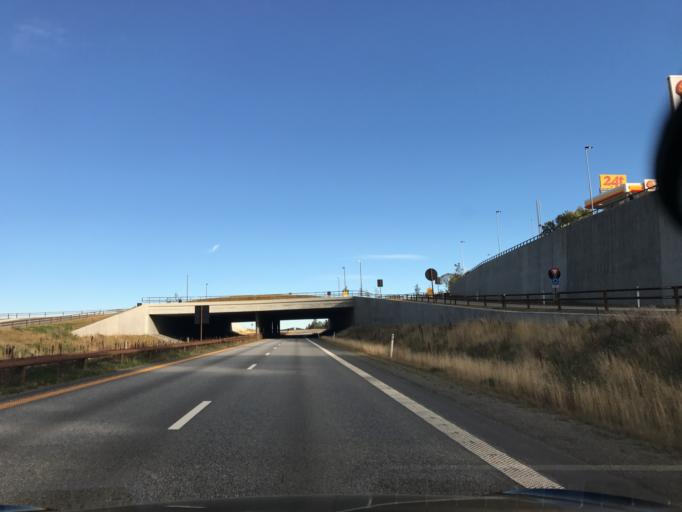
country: NO
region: Hedmark
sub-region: Stange
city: Stange
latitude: 60.5617
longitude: 11.2550
